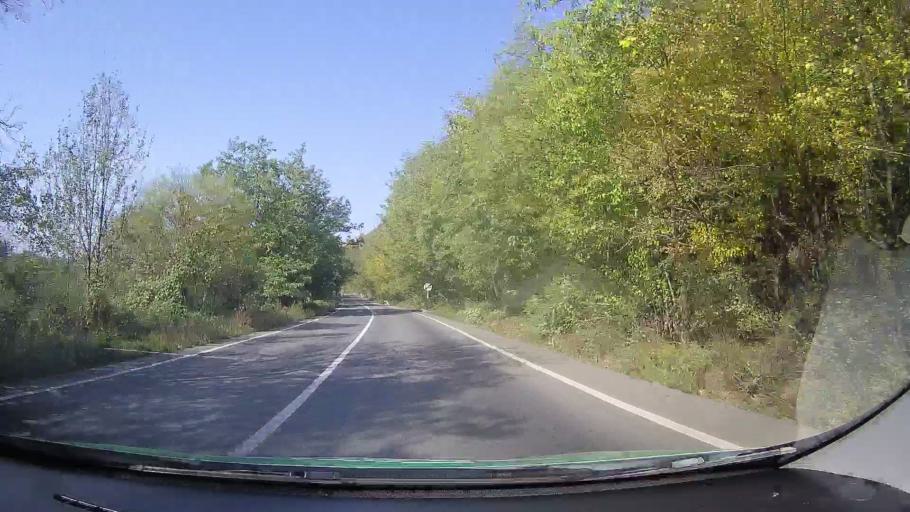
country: RO
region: Arad
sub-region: Comuna Savarsin
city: Savarsin
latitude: 45.9996
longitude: 22.2876
